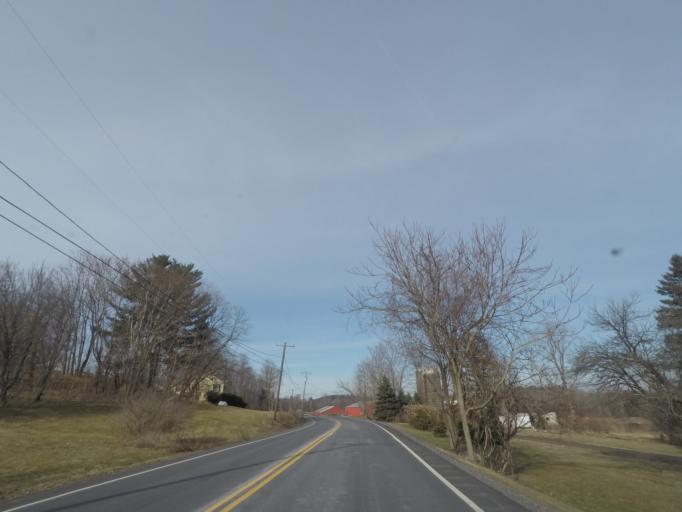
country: US
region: New York
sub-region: Columbia County
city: Valatie
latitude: 42.3895
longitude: -73.6431
